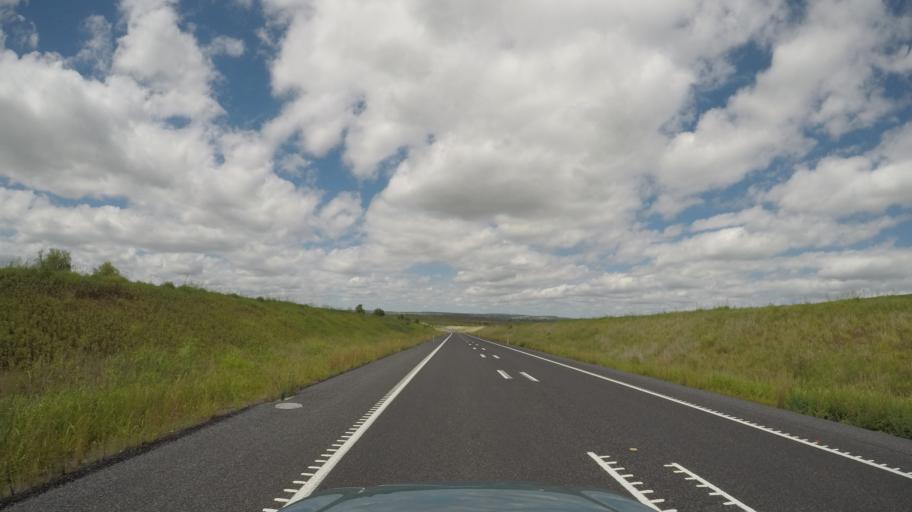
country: AU
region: Queensland
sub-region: Toowoomba
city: Westbrook
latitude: -27.5634
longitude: 151.8132
